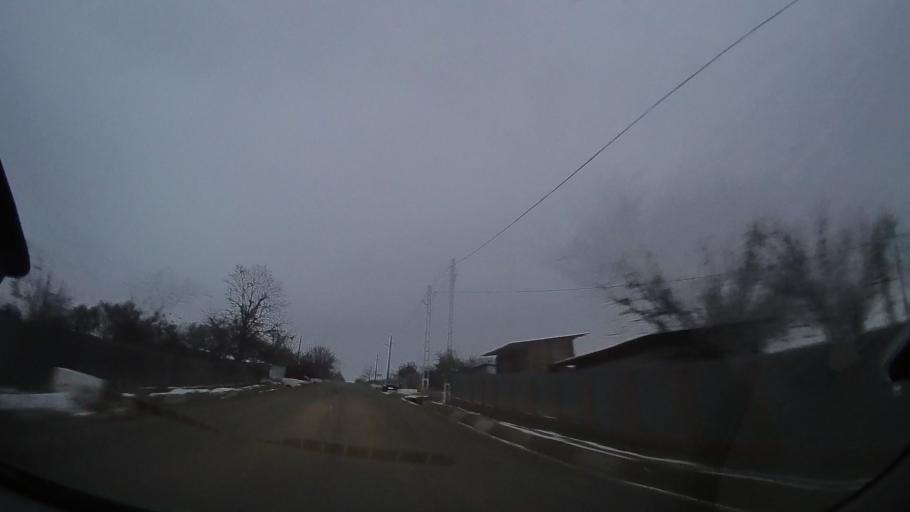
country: RO
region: Vaslui
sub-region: Comuna Gagesti
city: Gagesti
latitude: 46.3942
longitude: 27.9798
